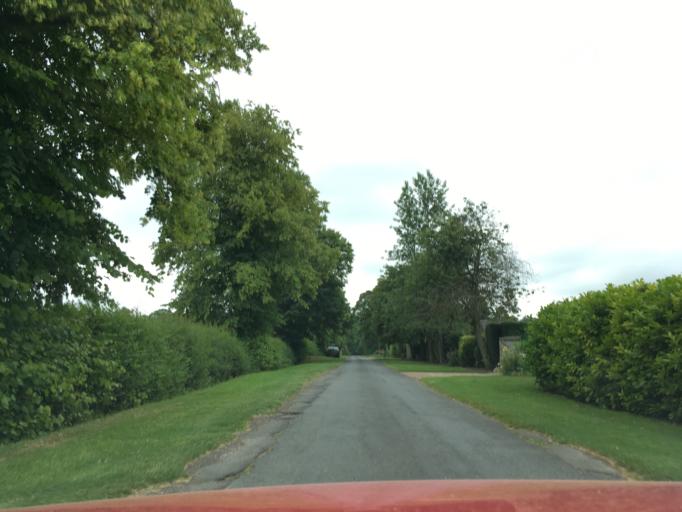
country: GB
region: England
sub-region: Oxfordshire
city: Somerton
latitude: 51.9983
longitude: -1.2491
